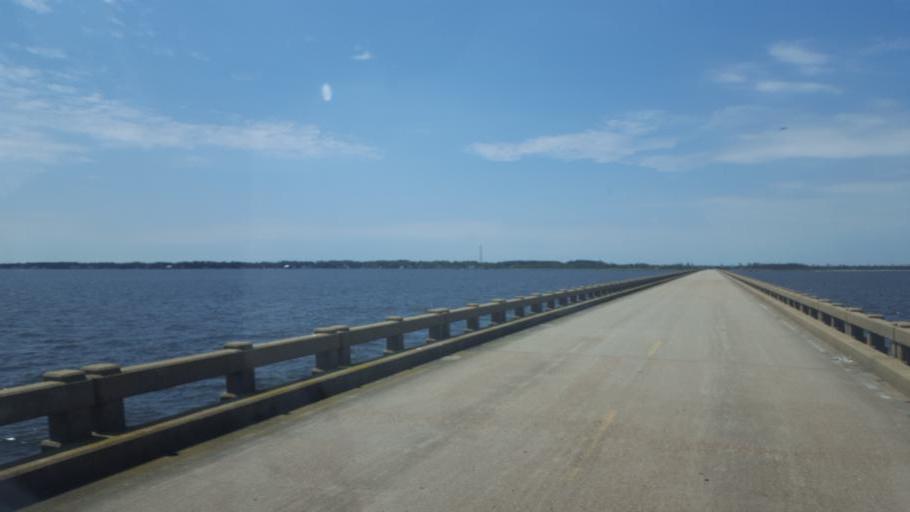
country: US
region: North Carolina
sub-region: Dare County
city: Manteo
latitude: 35.9165
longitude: -75.7553
